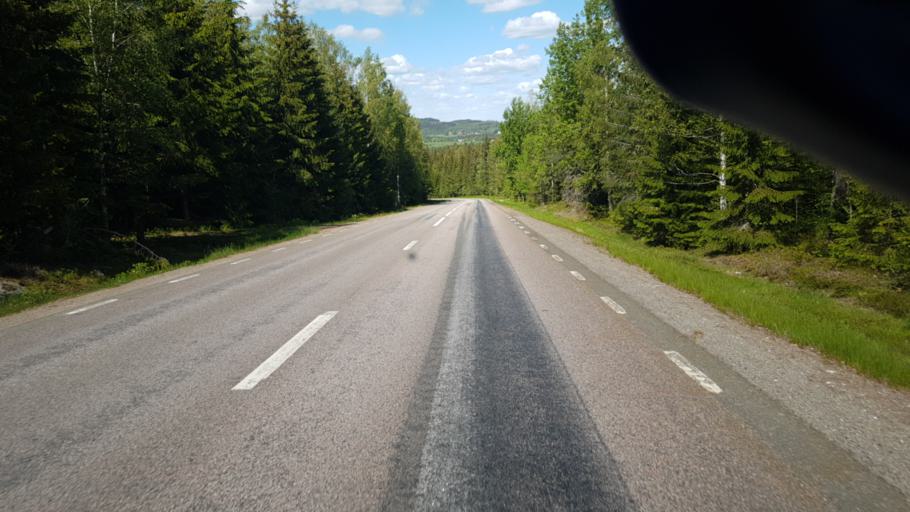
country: SE
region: Vaermland
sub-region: Sunne Kommun
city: Sunne
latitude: 59.7052
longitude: 13.1063
